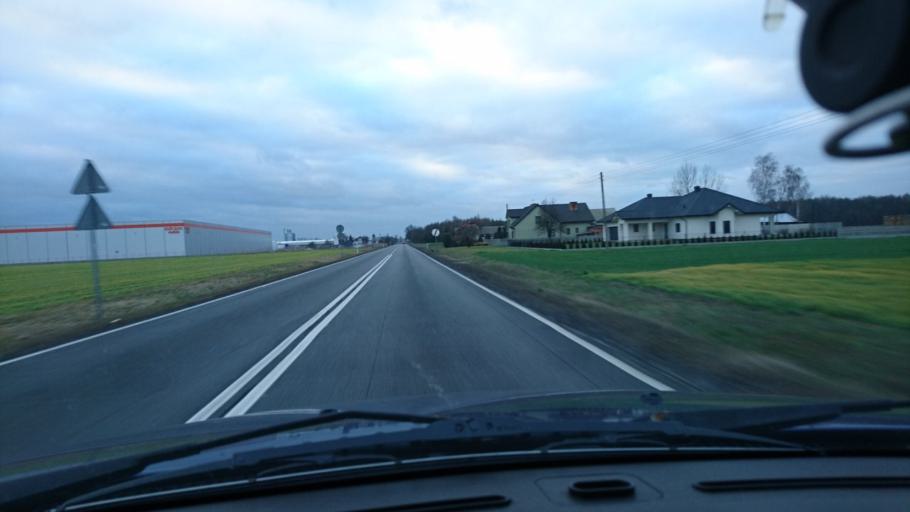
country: PL
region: Greater Poland Voivodeship
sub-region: Powiat kepinski
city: Leka Opatowska
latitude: 51.2245
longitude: 18.1061
